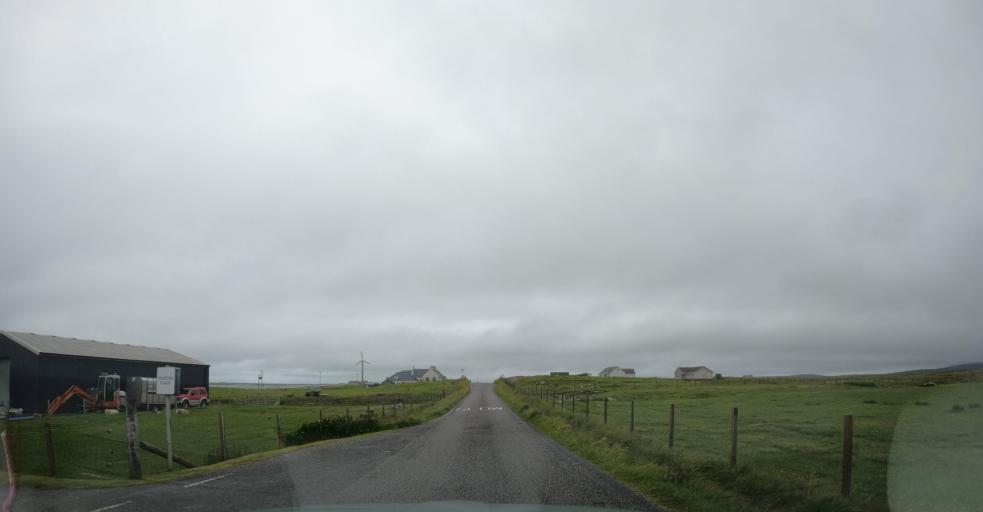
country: GB
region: Scotland
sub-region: Eilean Siar
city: Isle of North Uist
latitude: 57.5611
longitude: -7.3727
